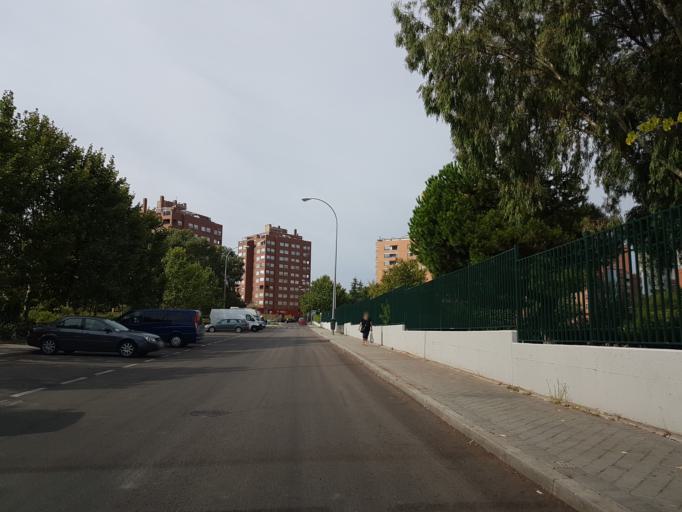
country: ES
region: Madrid
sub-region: Provincia de Madrid
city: Pinar de Chamartin
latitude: 40.4766
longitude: -3.6631
